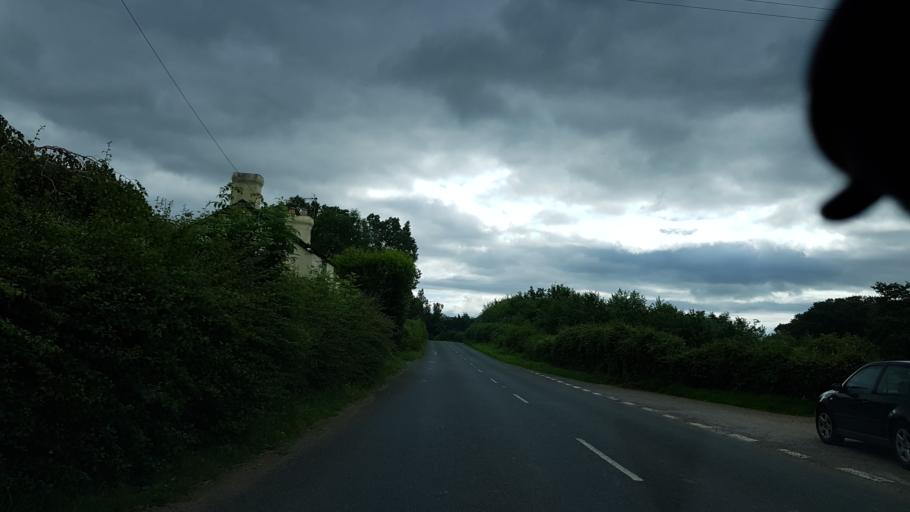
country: GB
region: Wales
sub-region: Monmouthshire
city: Llanarth
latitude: 51.7747
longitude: -2.8954
